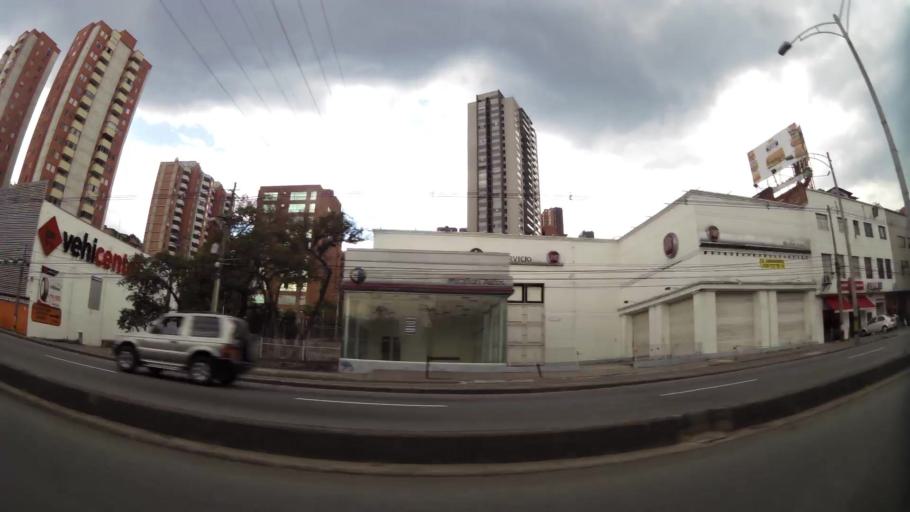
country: CO
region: Antioquia
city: Medellin
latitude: 6.2262
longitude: -75.5692
